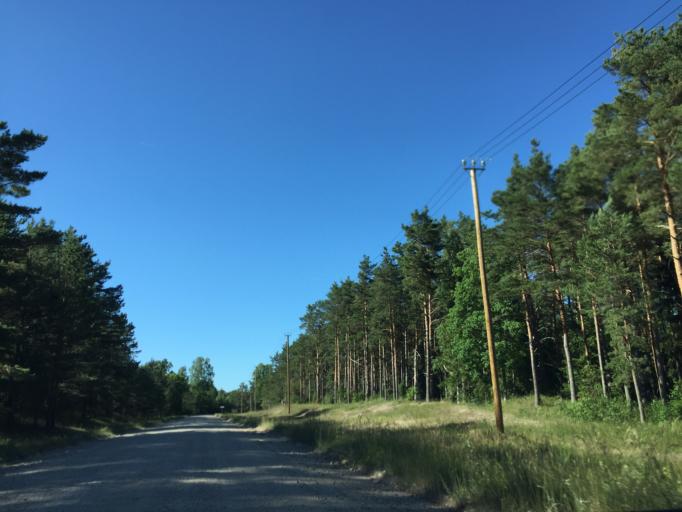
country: LV
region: Ventspils
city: Ventspils
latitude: 57.5679
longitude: 21.7226
